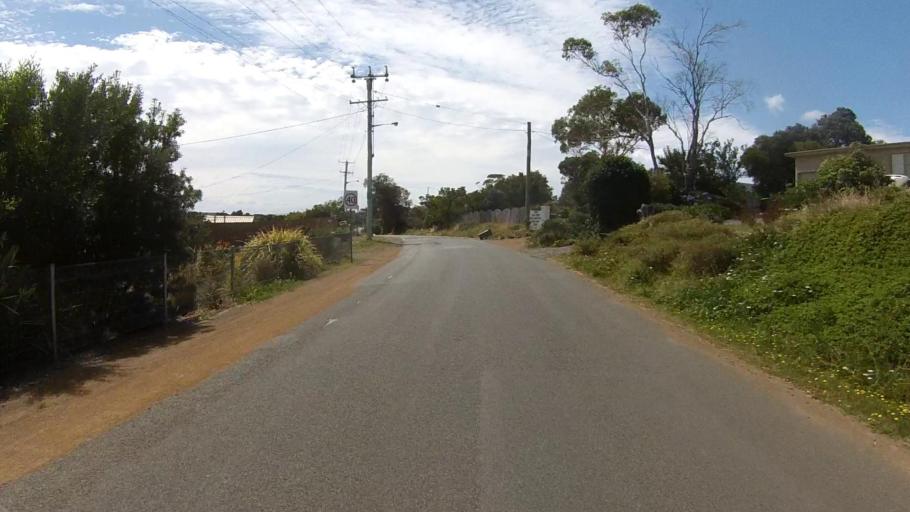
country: AU
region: Tasmania
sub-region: Kingborough
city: Taroona
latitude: -42.9932
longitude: 147.4035
